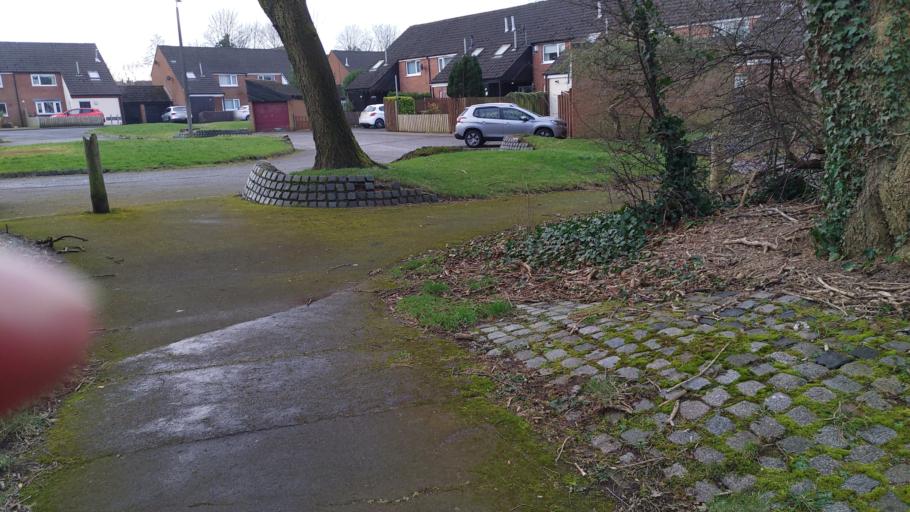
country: GB
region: England
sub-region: Lancashire
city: Clayton-le-Woods
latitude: 53.7110
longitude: -2.6375
